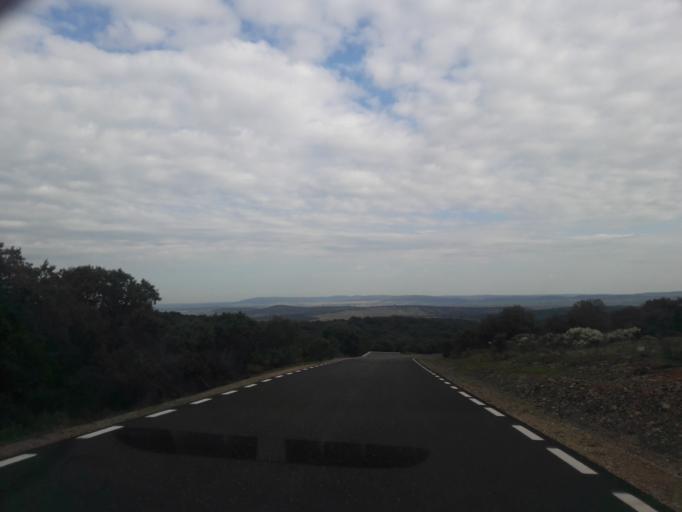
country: ES
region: Castille and Leon
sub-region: Provincia de Salamanca
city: Pastores
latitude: 40.5123
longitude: -6.5288
